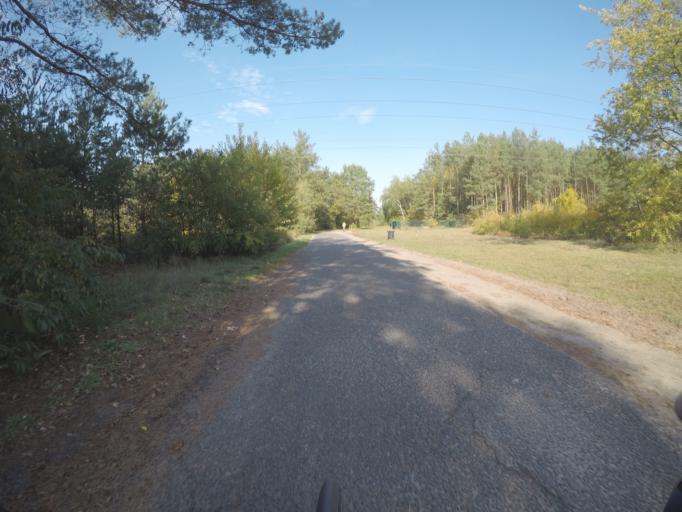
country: DE
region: Brandenburg
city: Hohen Neuendorf
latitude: 52.6720
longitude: 13.2408
